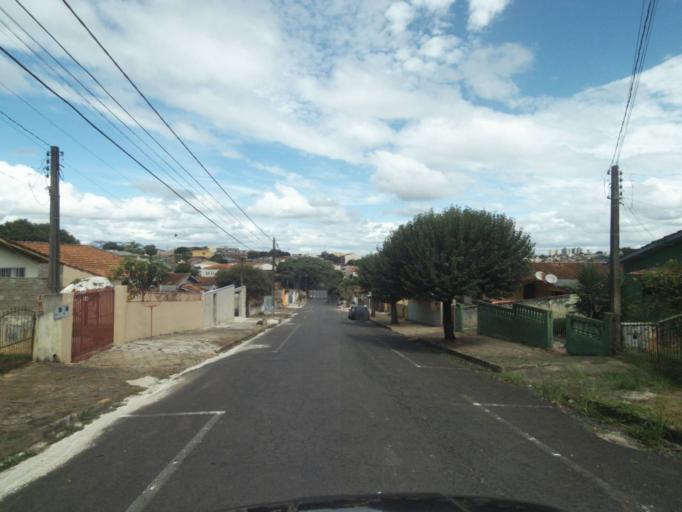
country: BR
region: Parana
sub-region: Telemaco Borba
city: Telemaco Borba
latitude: -24.3215
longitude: -50.6369
